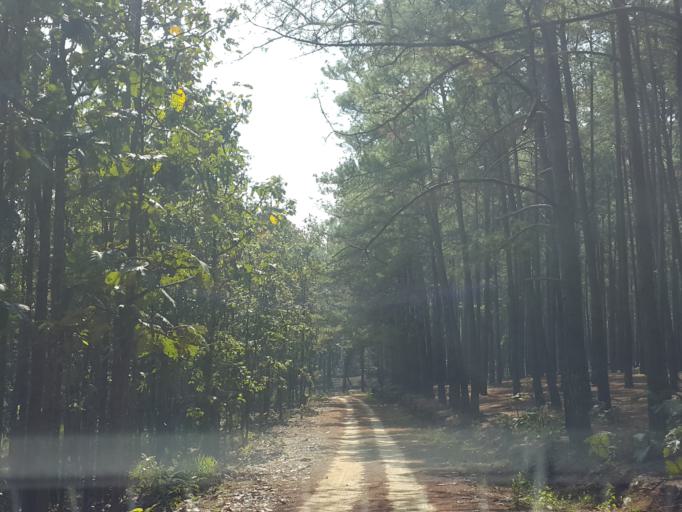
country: TH
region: Chiang Mai
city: Hot
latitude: 18.1453
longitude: 98.4320
